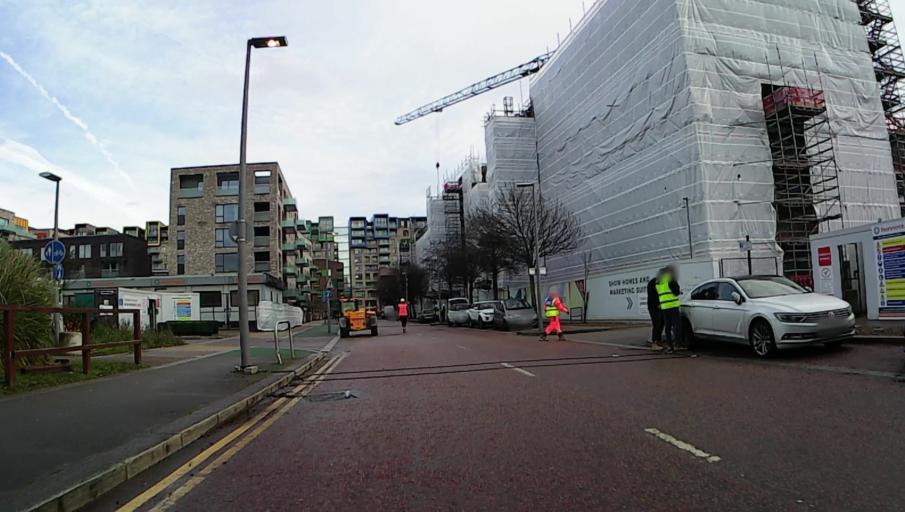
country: GB
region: England
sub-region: Greater London
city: Blackheath
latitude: 51.4925
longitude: 0.0161
